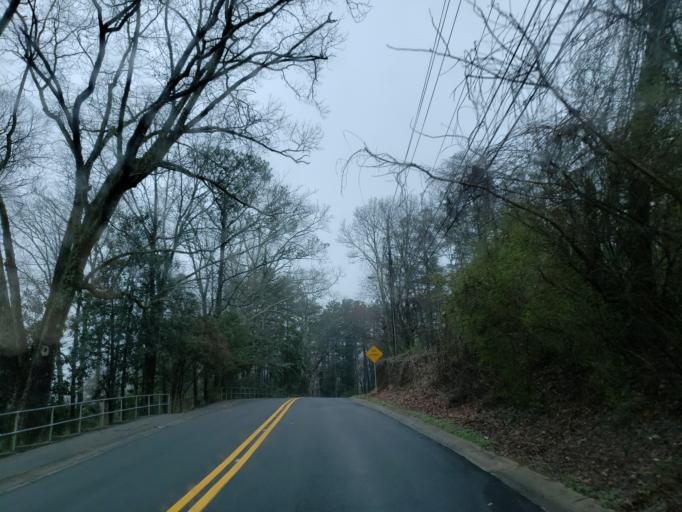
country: US
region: Georgia
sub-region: Cobb County
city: Marietta
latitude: 33.9332
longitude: -84.5714
